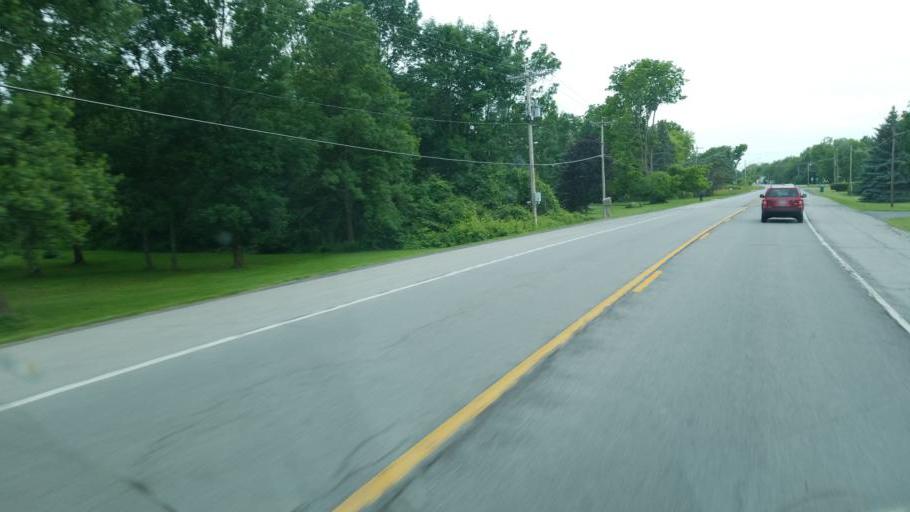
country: US
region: New York
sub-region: Genesee County
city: Oakfield
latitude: 42.9973
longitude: -78.2957
